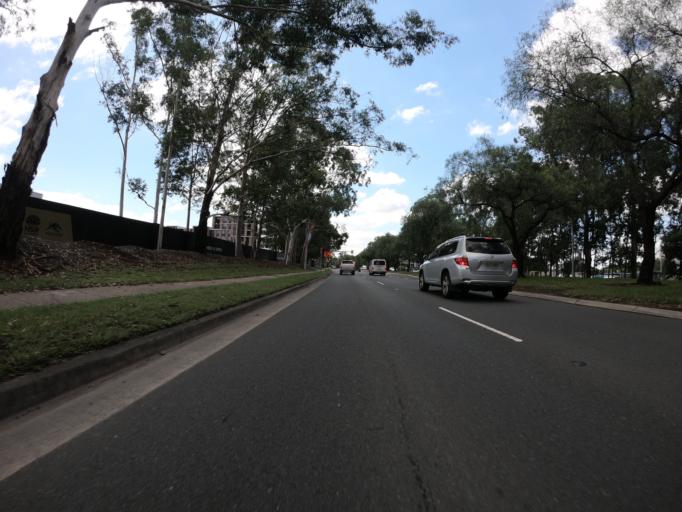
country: AU
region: New South Wales
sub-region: Penrith Municipality
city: Penrith
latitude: -33.7579
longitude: 150.6856
